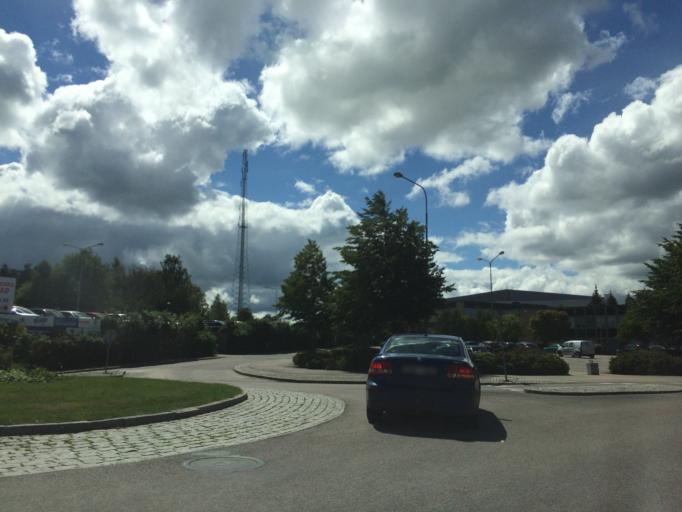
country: SE
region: Vaestra Goetaland
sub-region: Trollhattan
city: Trollhattan
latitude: 58.2810
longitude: 12.3023
